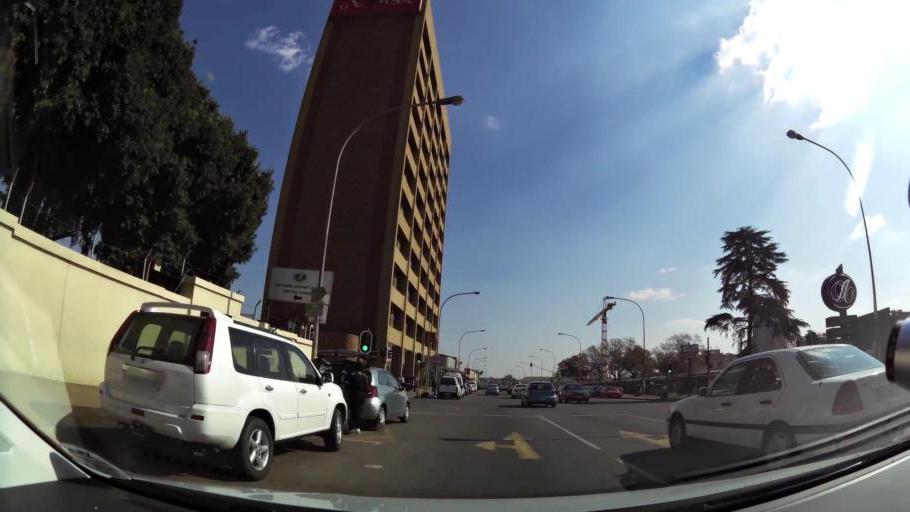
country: ZA
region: Gauteng
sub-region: City of Johannesburg Metropolitan Municipality
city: Modderfontein
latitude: -26.1075
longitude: 28.2331
